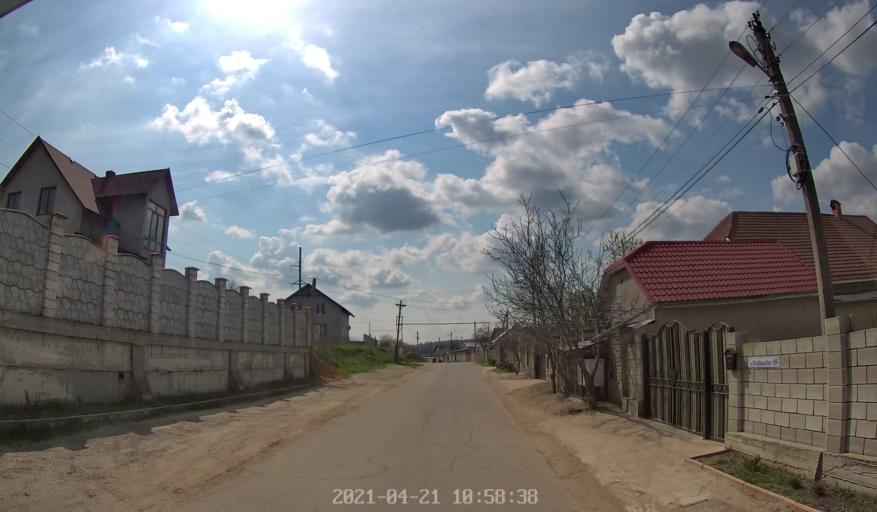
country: MD
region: Chisinau
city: Singera
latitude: 46.9527
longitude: 28.9427
